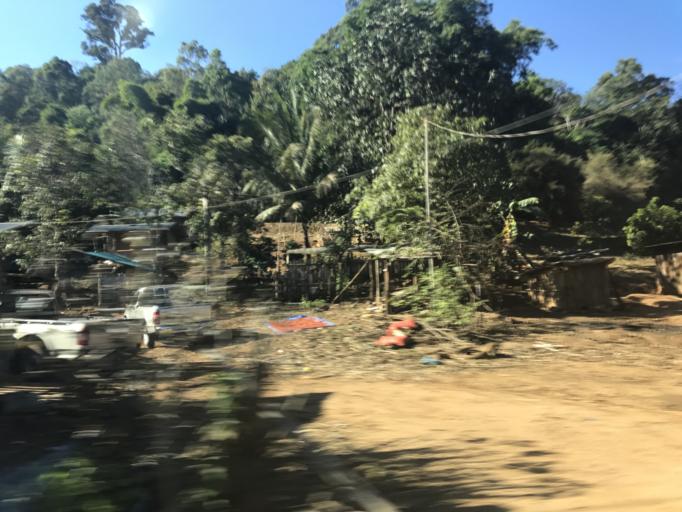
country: TH
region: Tak
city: Phop Phra
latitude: 16.5679
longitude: 98.8156
